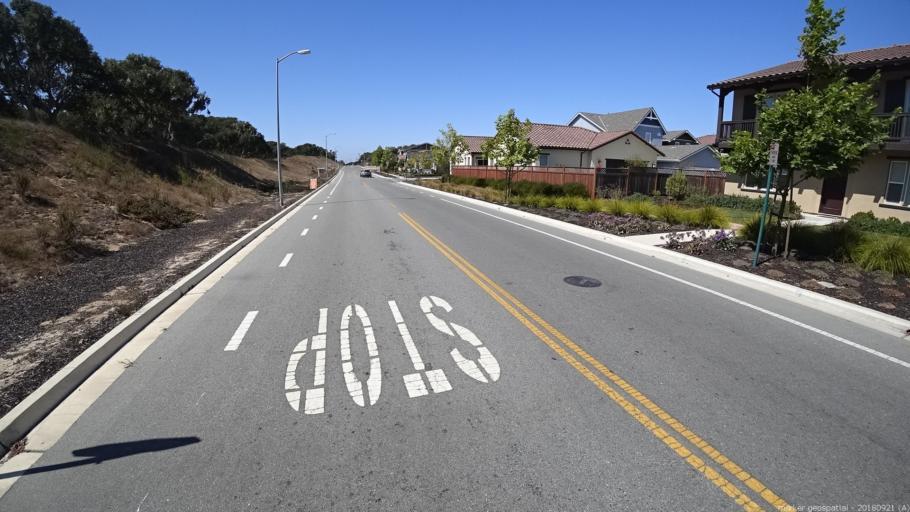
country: US
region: California
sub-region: Monterey County
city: Marina
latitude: 36.6553
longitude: -121.7420
